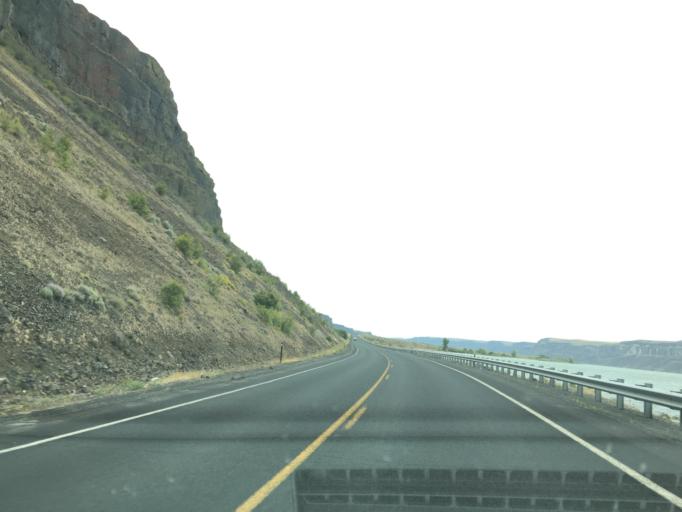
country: US
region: Washington
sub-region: Okanogan County
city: Coulee Dam
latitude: 47.7995
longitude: -119.1843
